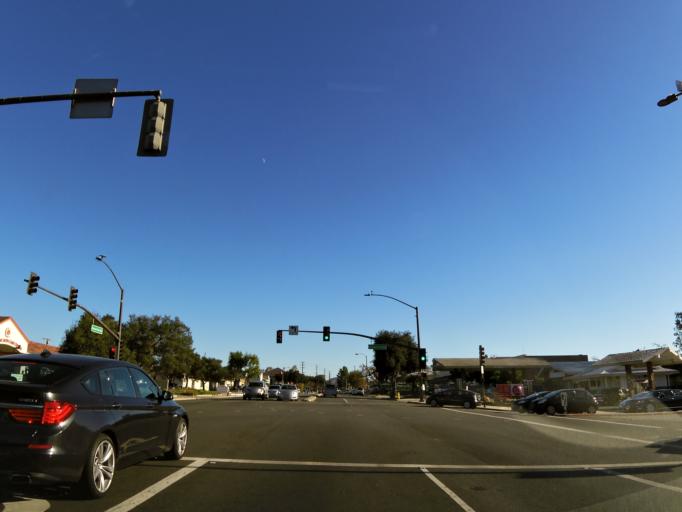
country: US
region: California
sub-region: Ventura County
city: Thousand Oaks
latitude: 34.1693
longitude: -118.8364
